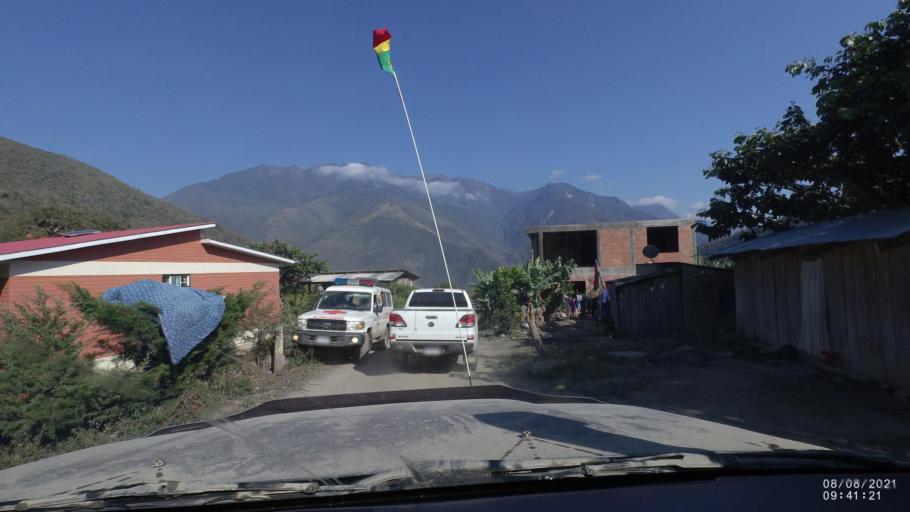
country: BO
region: La Paz
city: Quime
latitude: -16.5999
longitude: -66.7137
